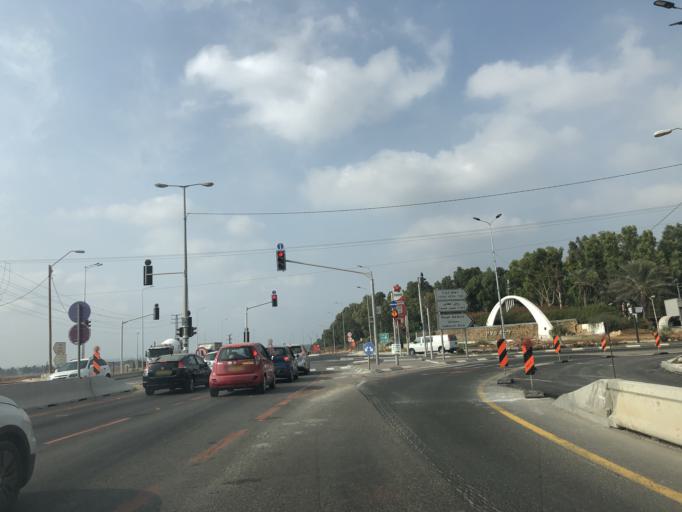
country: IL
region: Central District
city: Rosh Ha'Ayin
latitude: 32.0927
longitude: 34.9409
